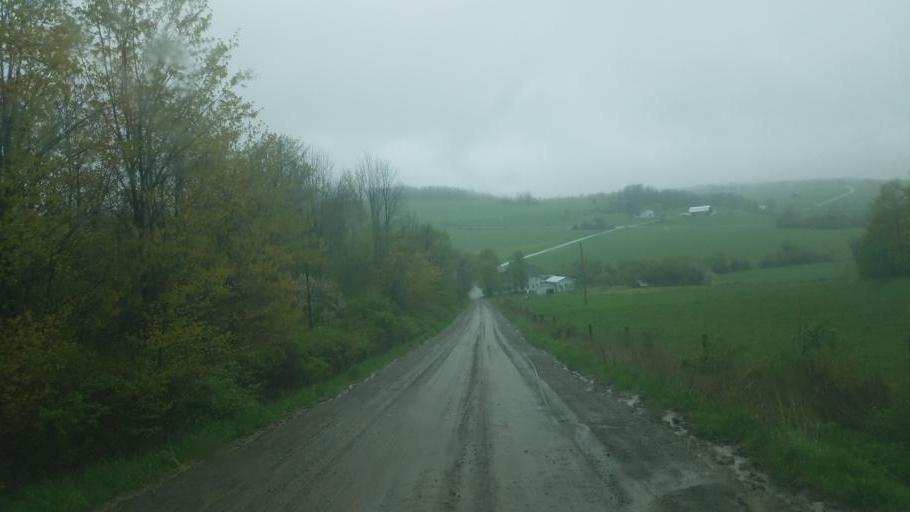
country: US
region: Pennsylvania
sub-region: Tioga County
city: Westfield
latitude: 42.1015
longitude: -77.5169
